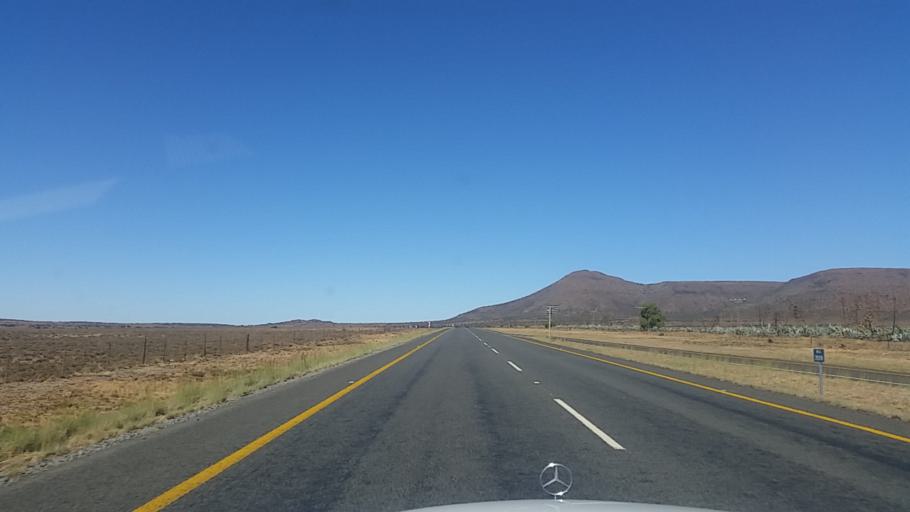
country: ZA
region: Eastern Cape
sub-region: Cacadu District Municipality
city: Graaff-Reinet
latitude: -32.0239
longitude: 24.6346
